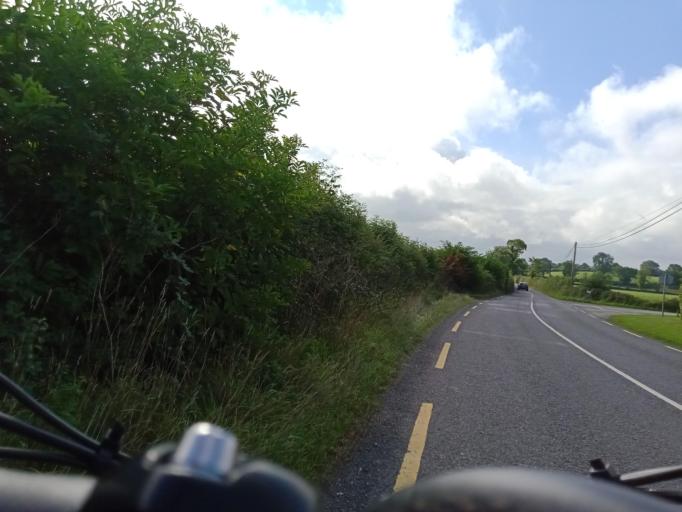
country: IE
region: Leinster
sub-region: Kilkenny
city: Kilkenny
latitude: 52.5744
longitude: -7.2777
